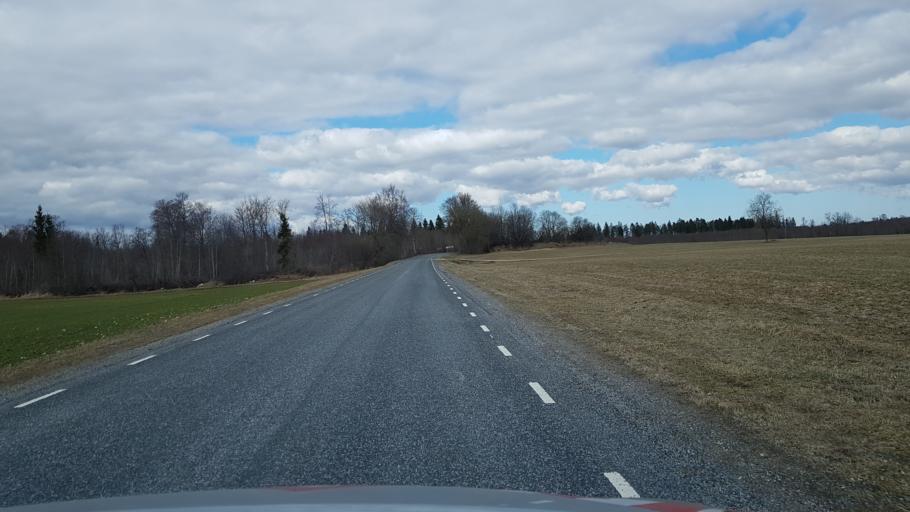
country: EE
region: Laeaene-Virumaa
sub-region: Tamsalu vald
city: Tamsalu
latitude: 59.1819
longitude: 26.1276
